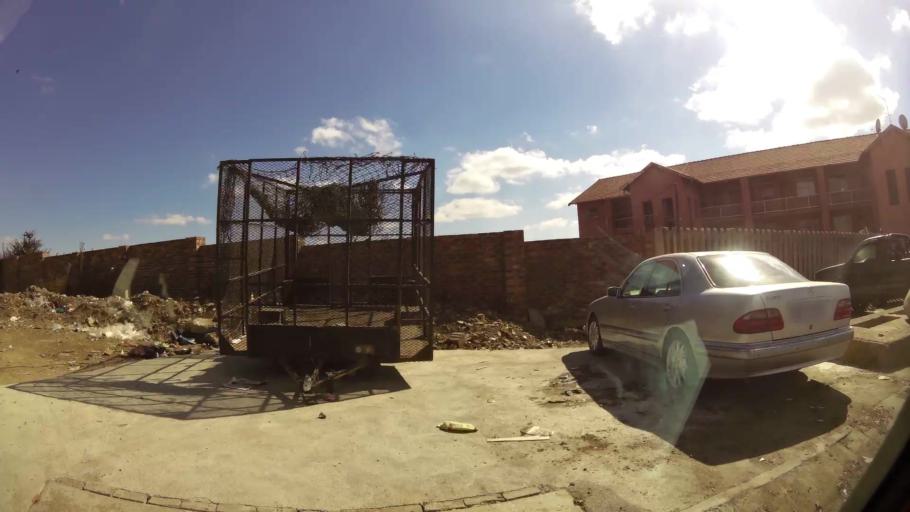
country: ZA
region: Gauteng
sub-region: City of Johannesburg Metropolitan Municipality
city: Midrand
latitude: -26.0288
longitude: 28.1731
